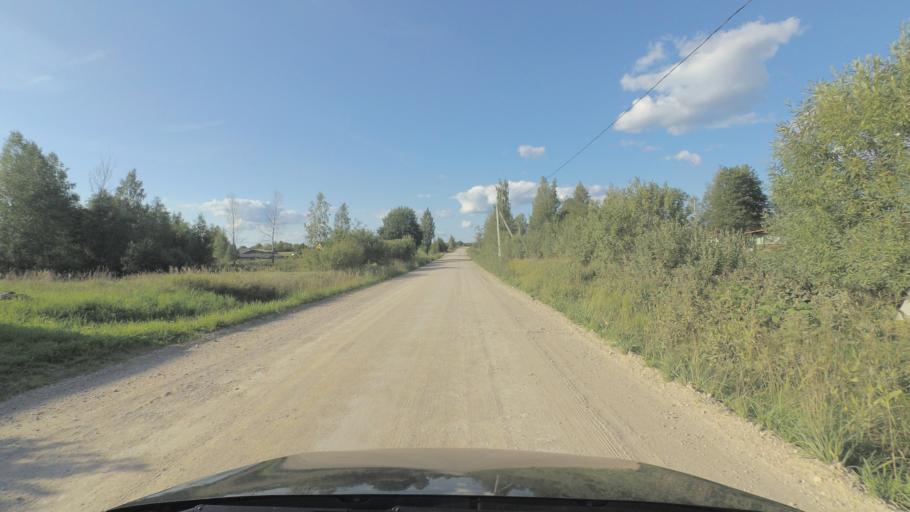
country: LT
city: Pabrade
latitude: 55.1255
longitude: 25.7054
